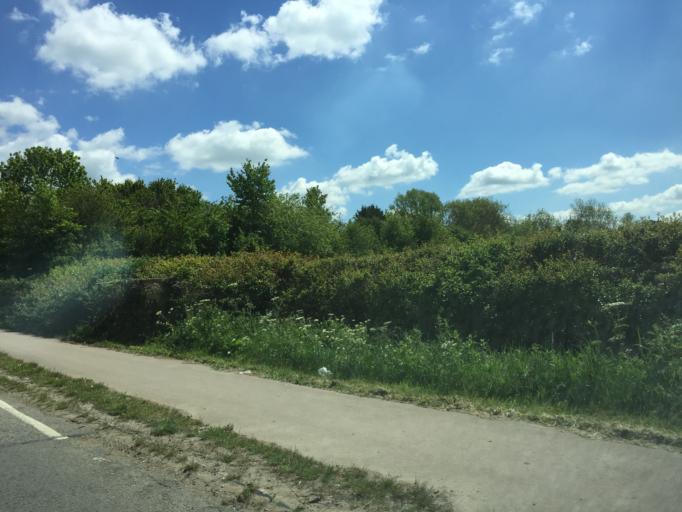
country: GB
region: England
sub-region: Milton Keynes
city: Wavendon
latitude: 52.0286
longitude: -0.6706
